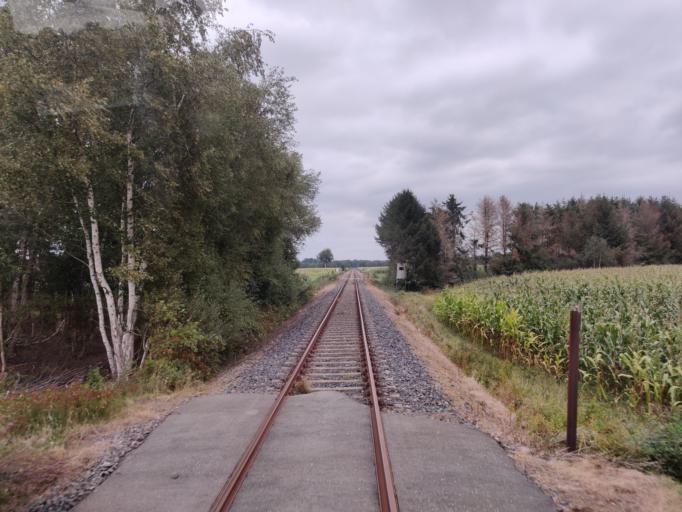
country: DE
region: Lower Saxony
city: Vollersode
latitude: 53.2825
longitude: 8.9668
